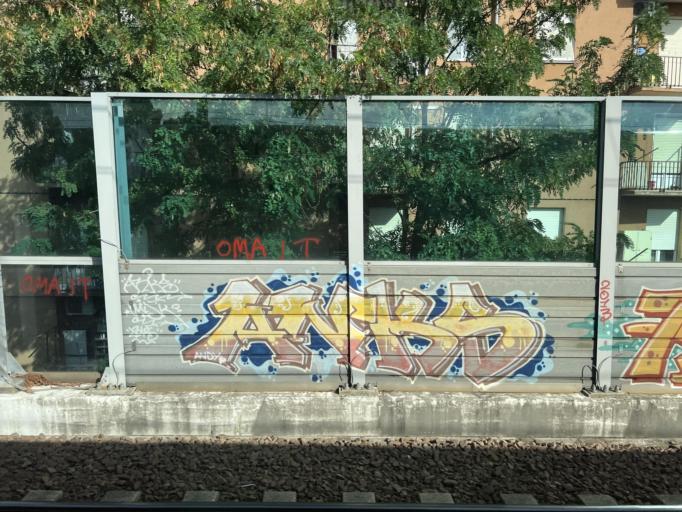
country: IT
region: Emilia-Romagna
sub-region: Provincia di Parma
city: Parma
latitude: 44.8095
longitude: 10.3463
